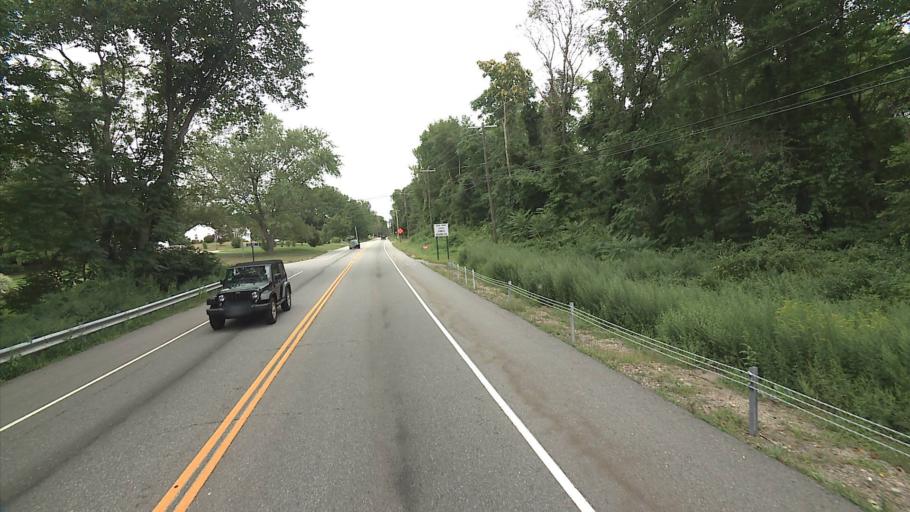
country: US
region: Connecticut
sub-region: New London County
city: Montville Center
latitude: 41.4467
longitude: -72.2327
